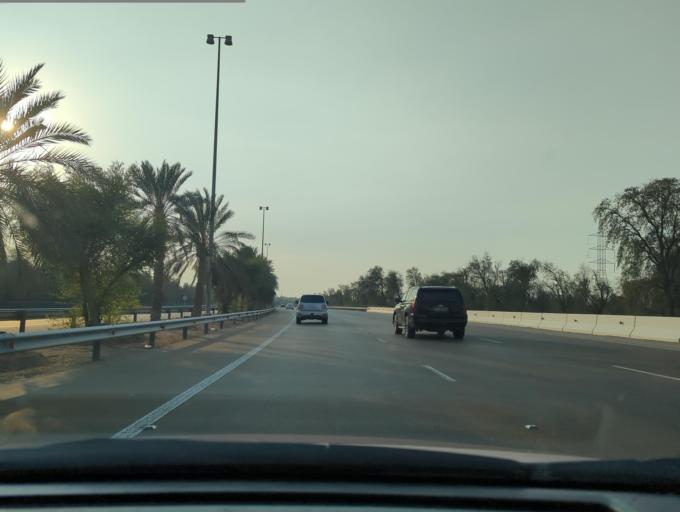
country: AE
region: Abu Dhabi
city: Al Ain
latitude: 24.1703
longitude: 55.2644
